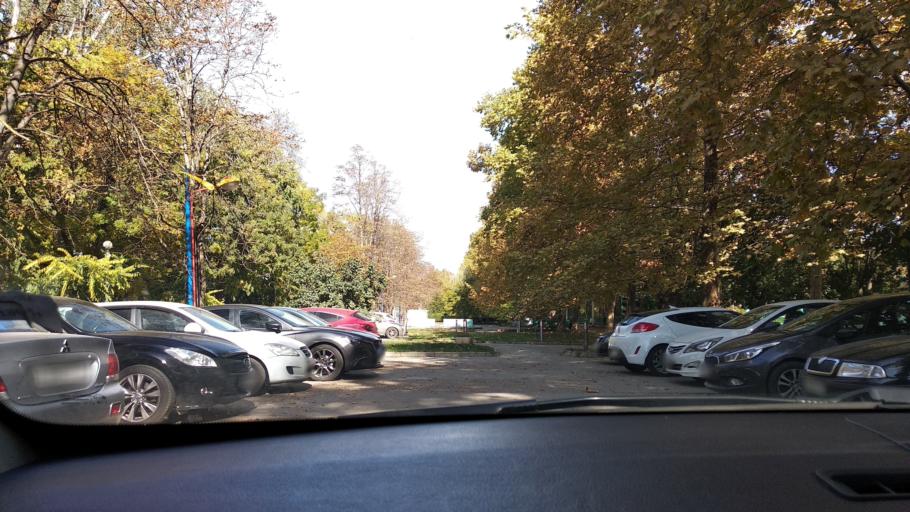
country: RU
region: Adygeya
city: Yablonovskiy
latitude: 45.0182
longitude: 38.9539
